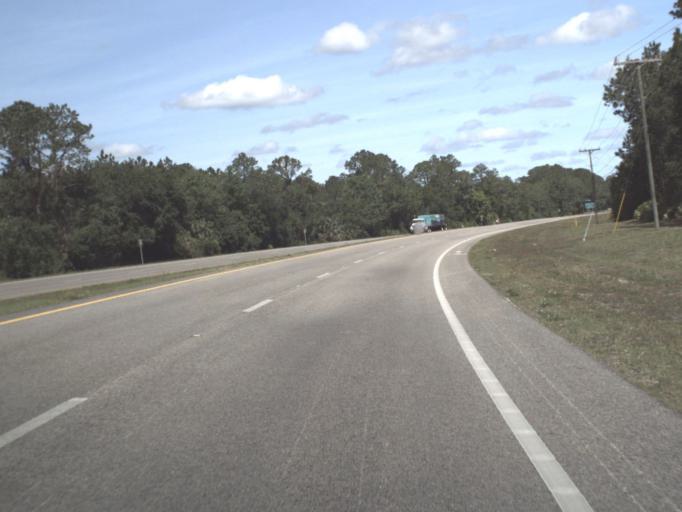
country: US
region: Florida
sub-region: Flagler County
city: Bunnell
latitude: 29.4323
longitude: -81.2309
